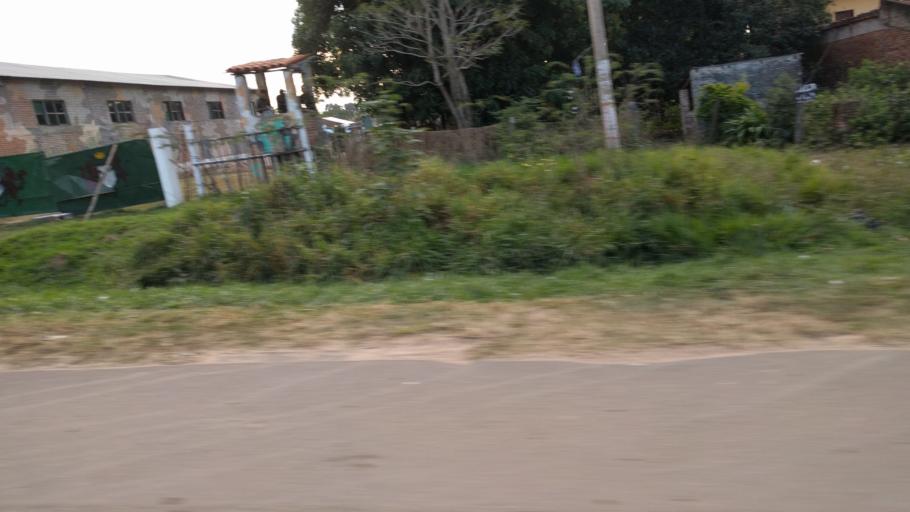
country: BO
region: Santa Cruz
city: Buena Vista
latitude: -17.4526
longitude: -63.6542
